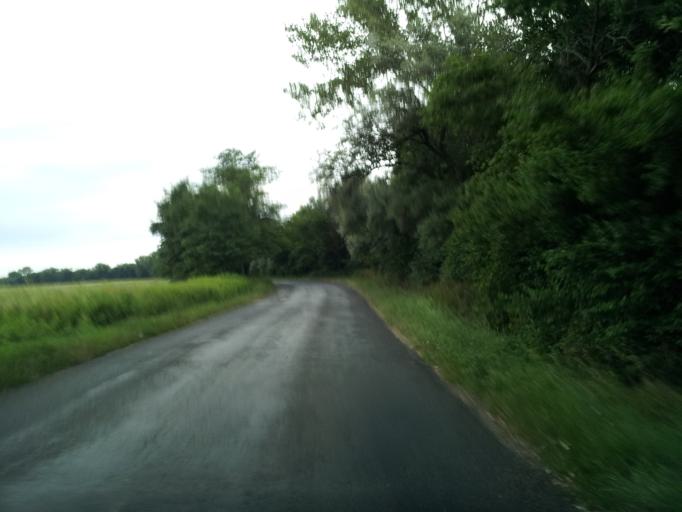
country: HU
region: Veszprem
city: Devecser
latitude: 47.1061
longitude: 17.4093
